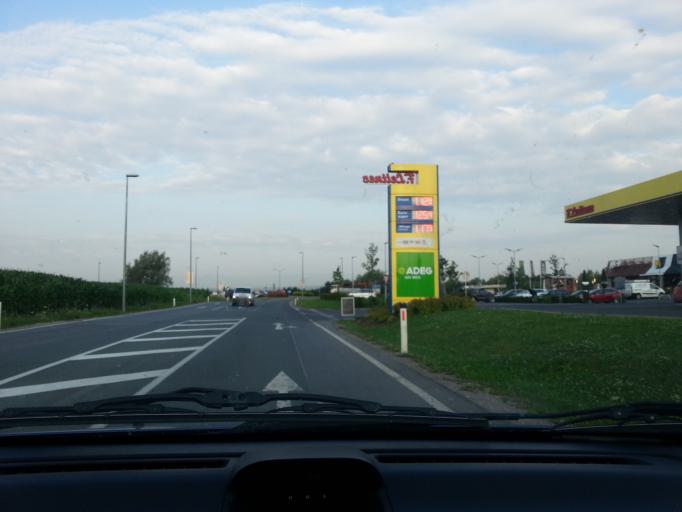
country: AT
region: Styria
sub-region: Politischer Bezirk Graz-Umgebung
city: Feldkirchen bei Graz
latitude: 47.0082
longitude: 15.4404
